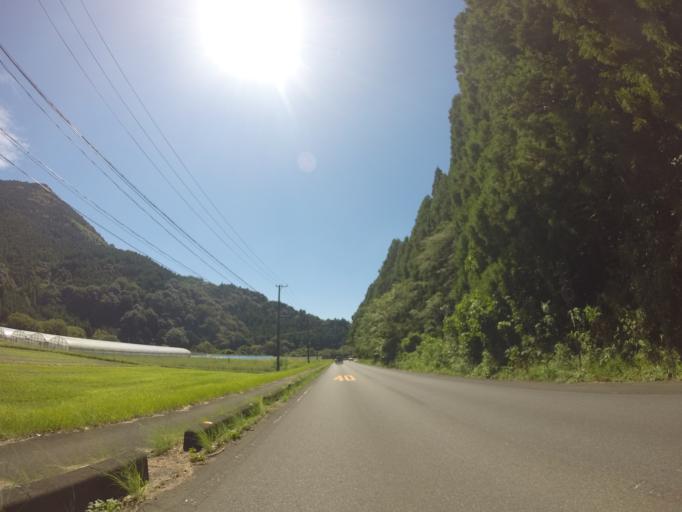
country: JP
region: Shizuoka
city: Fujieda
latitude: 34.9520
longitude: 138.2120
